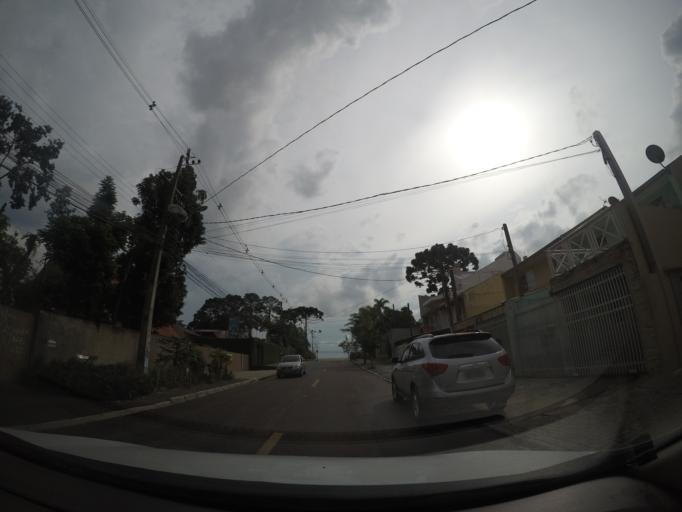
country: BR
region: Parana
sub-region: Sao Jose Dos Pinhais
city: Sao Jose dos Pinhais
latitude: -25.5208
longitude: -49.2541
